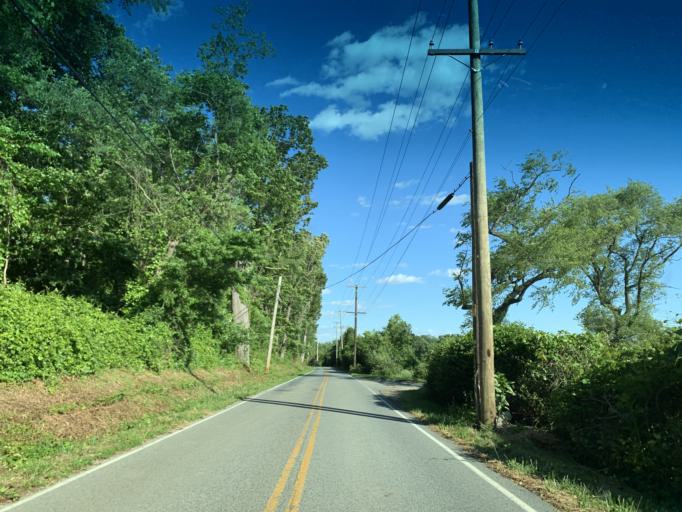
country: US
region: Maryland
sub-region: Cecil County
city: Perryville
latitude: 39.5951
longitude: -76.0882
